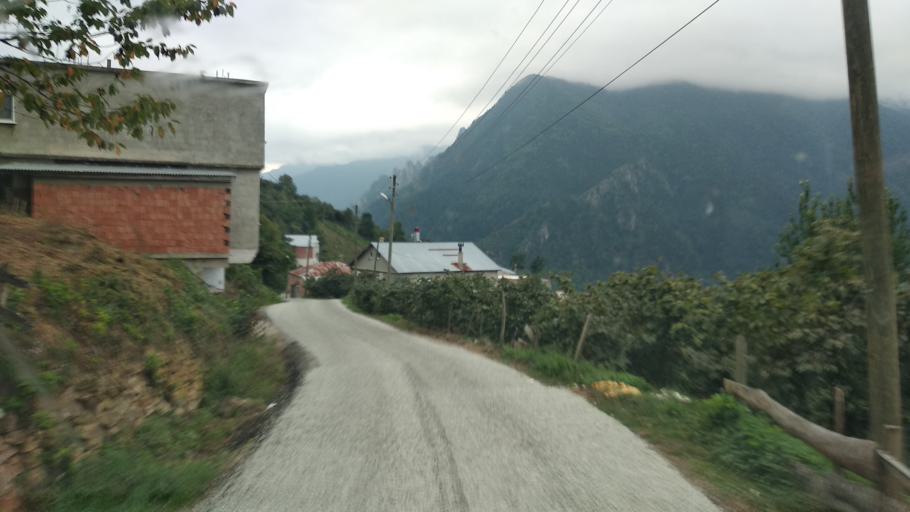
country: TR
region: Giresun
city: Dogankent
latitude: 40.7457
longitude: 38.9898
